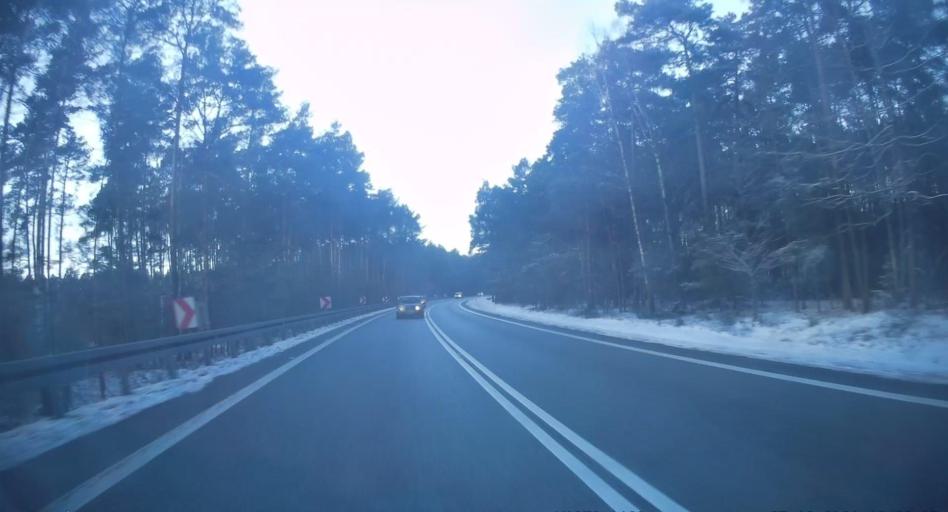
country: PL
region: Swietokrzyskie
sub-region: Powiat konecki
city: Ruda Maleniecka
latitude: 51.1661
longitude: 20.2236
